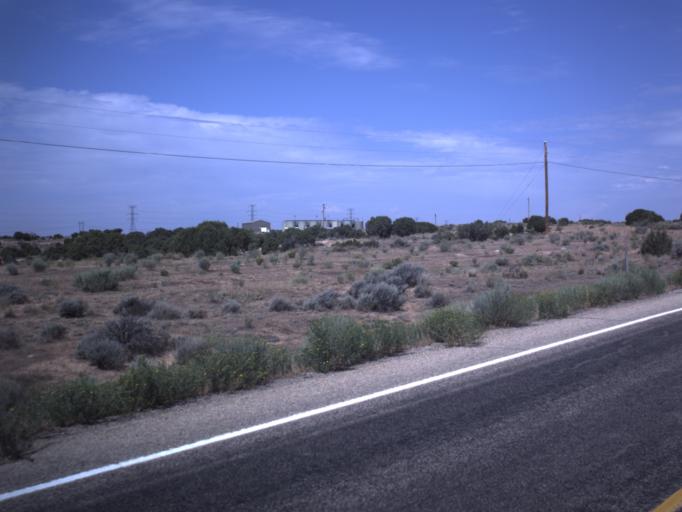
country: US
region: Utah
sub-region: Uintah County
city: Naples
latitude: 40.1731
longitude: -109.3207
